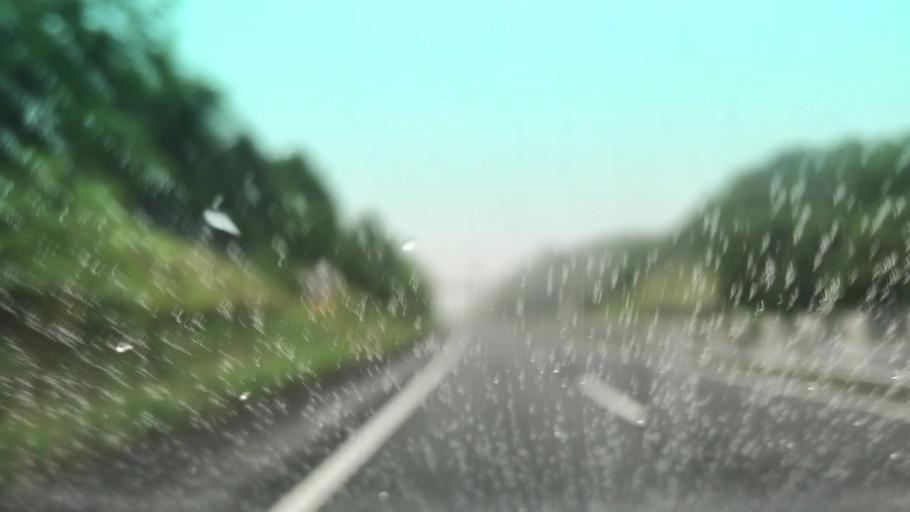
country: JP
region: Hokkaido
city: Tomakomai
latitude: 42.6265
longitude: 141.4829
